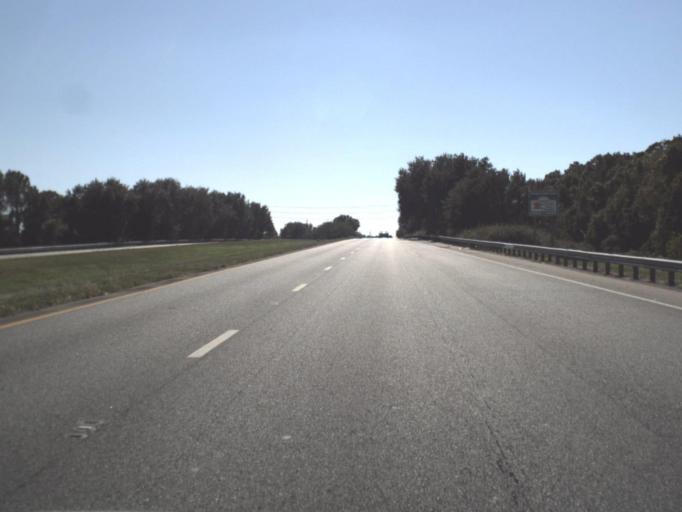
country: US
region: Florida
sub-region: Seminole County
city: Oviedo
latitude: 28.6512
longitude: -81.2352
